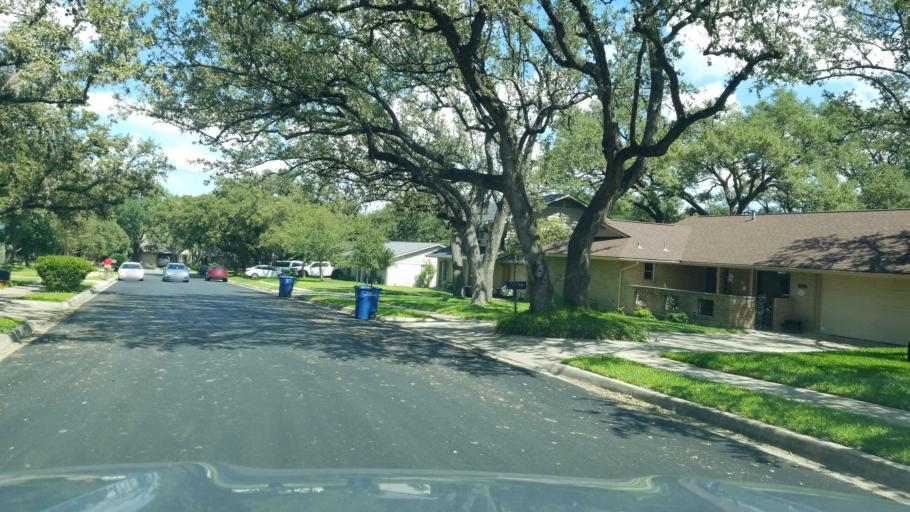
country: US
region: Texas
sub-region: Bexar County
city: Castle Hills
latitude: 29.5466
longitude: -98.5022
